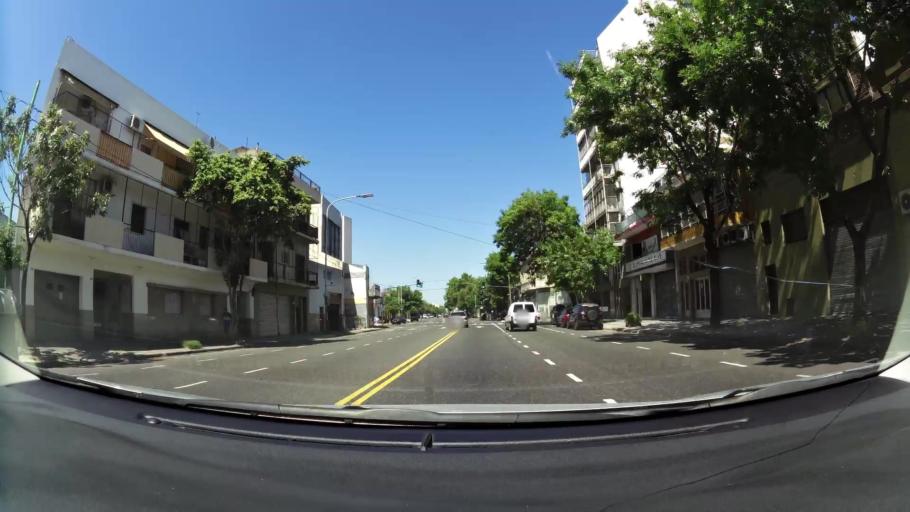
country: AR
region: Buenos Aires F.D.
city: Buenos Aires
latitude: -34.6380
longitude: -58.4169
